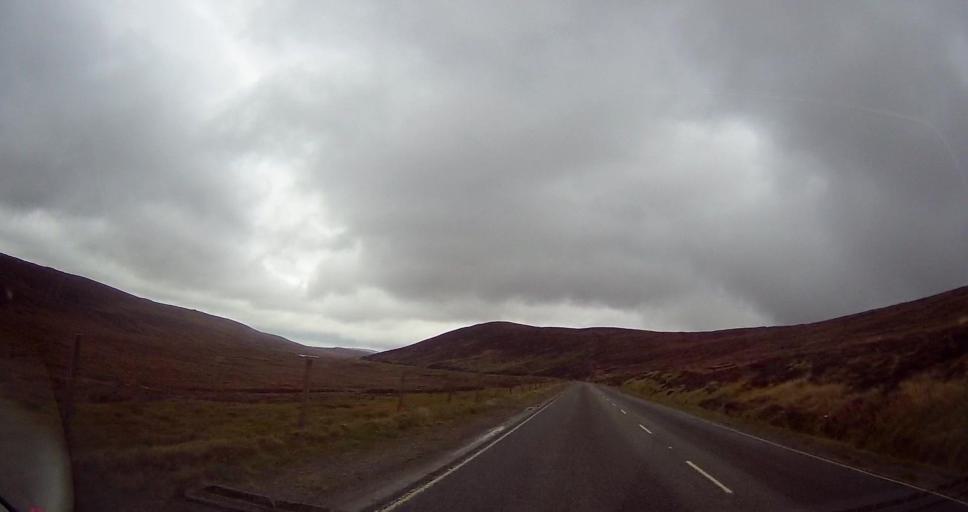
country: GB
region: Scotland
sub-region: Shetland Islands
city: Lerwick
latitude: 60.2980
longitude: -1.2394
